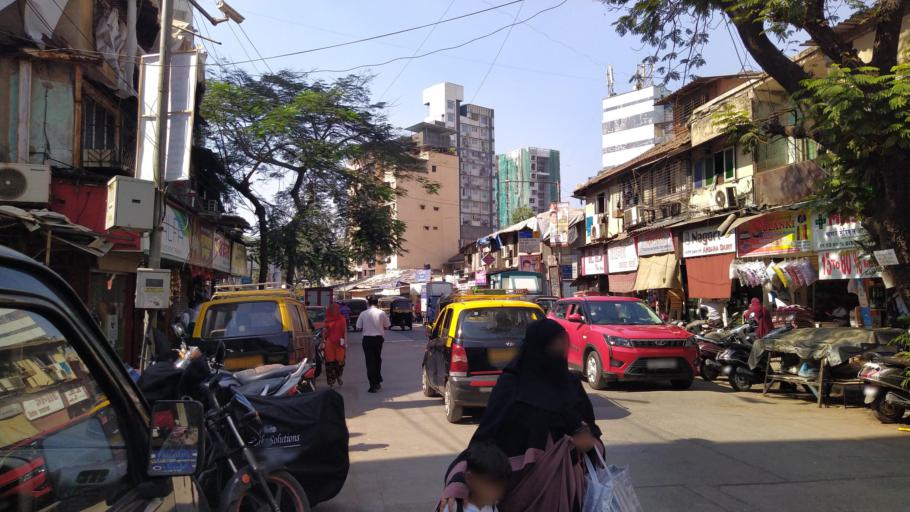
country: IN
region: Maharashtra
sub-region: Mumbai Suburban
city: Mumbai
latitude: 19.0656
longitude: 72.8762
